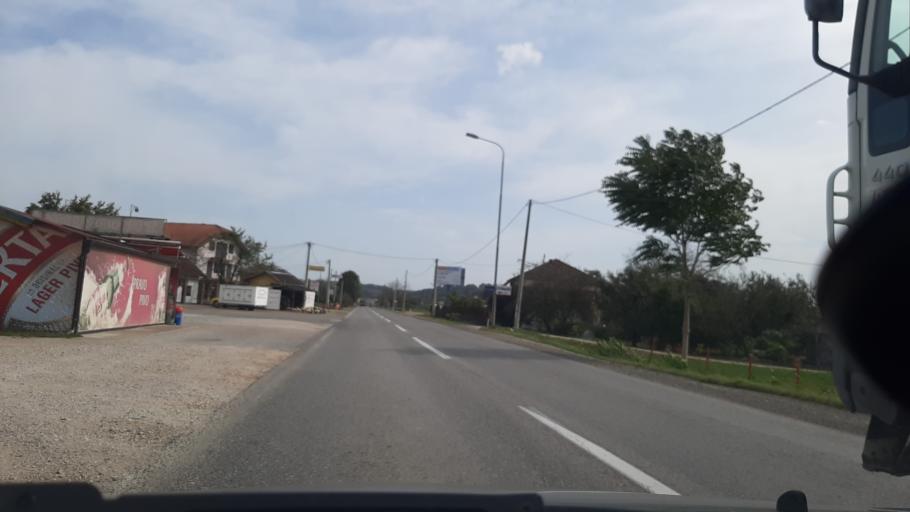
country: BA
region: Republika Srpska
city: Laktasi
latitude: 44.8776
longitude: 17.2973
